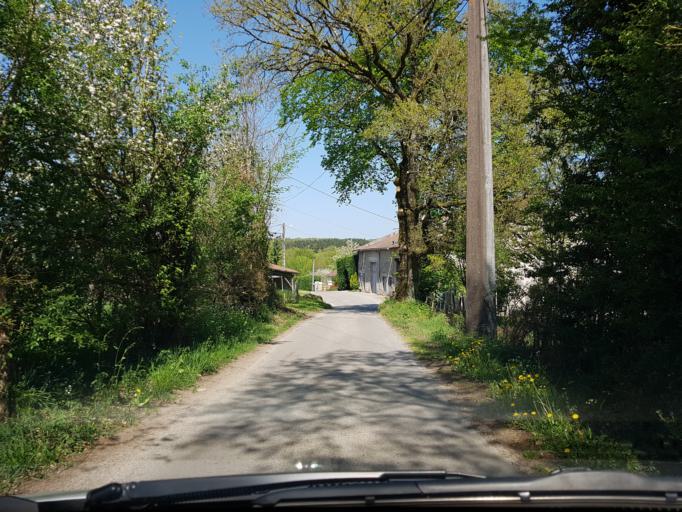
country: FR
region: Limousin
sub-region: Departement de la Haute-Vienne
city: Saint-Junien
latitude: 45.9019
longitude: 0.9055
